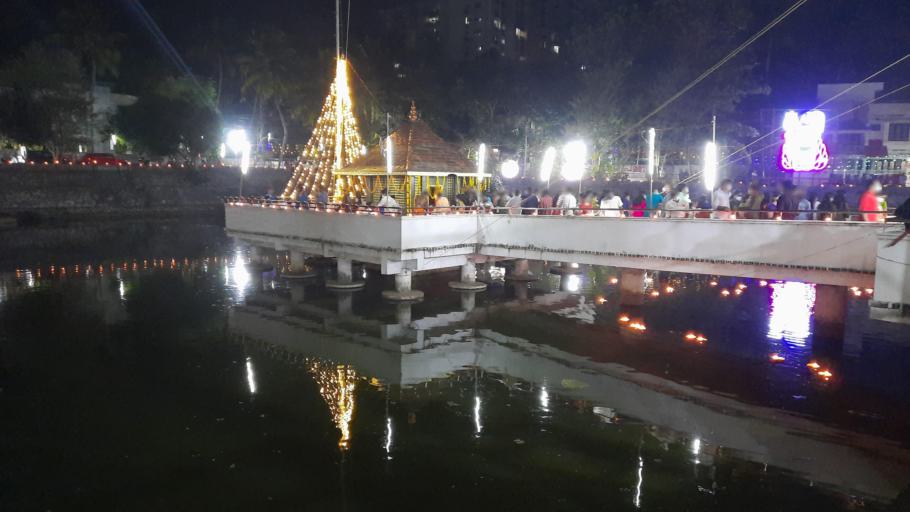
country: IN
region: Kerala
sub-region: Thiruvananthapuram
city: Thiruvananthapuram
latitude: 8.5475
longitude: 76.9198
